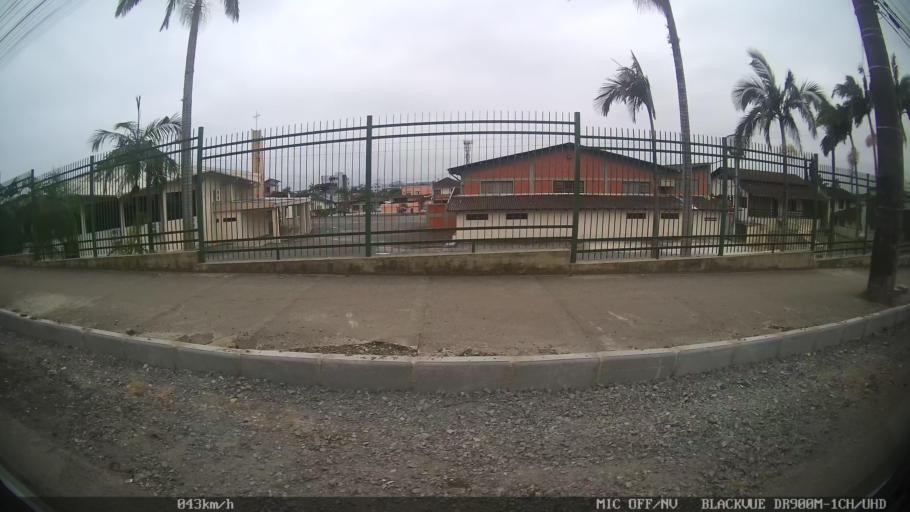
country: BR
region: Santa Catarina
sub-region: Joinville
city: Joinville
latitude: -26.2988
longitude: -48.8219
